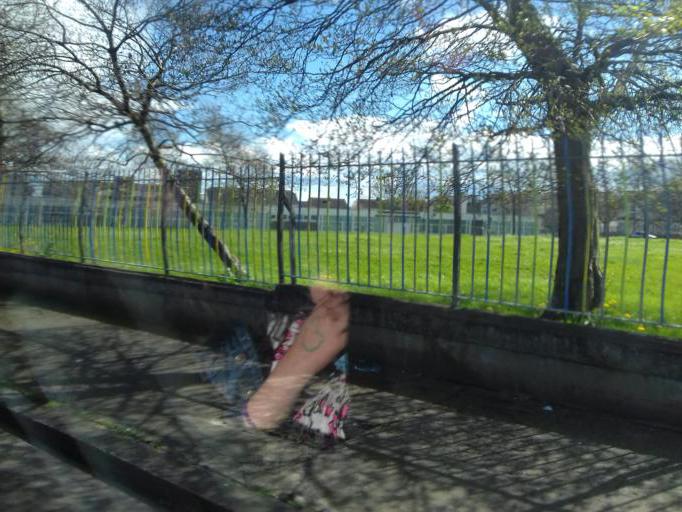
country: IE
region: Leinster
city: Donaghmede
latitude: 53.3890
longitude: -6.1633
